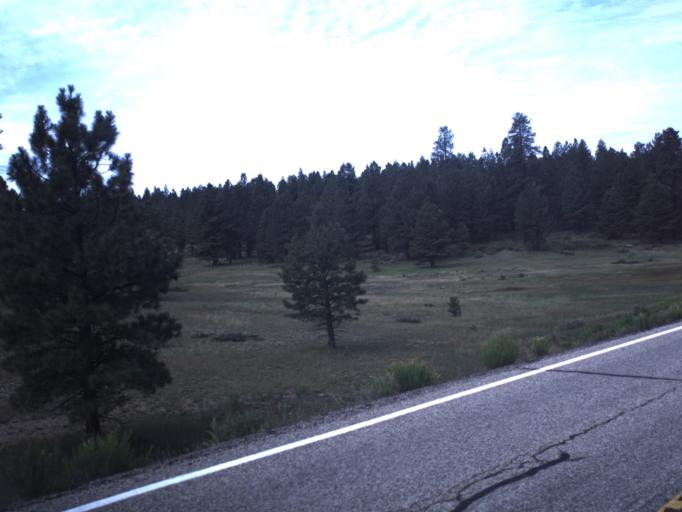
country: US
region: Utah
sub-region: Garfield County
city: Panguitch
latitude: 37.4908
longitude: -112.5681
